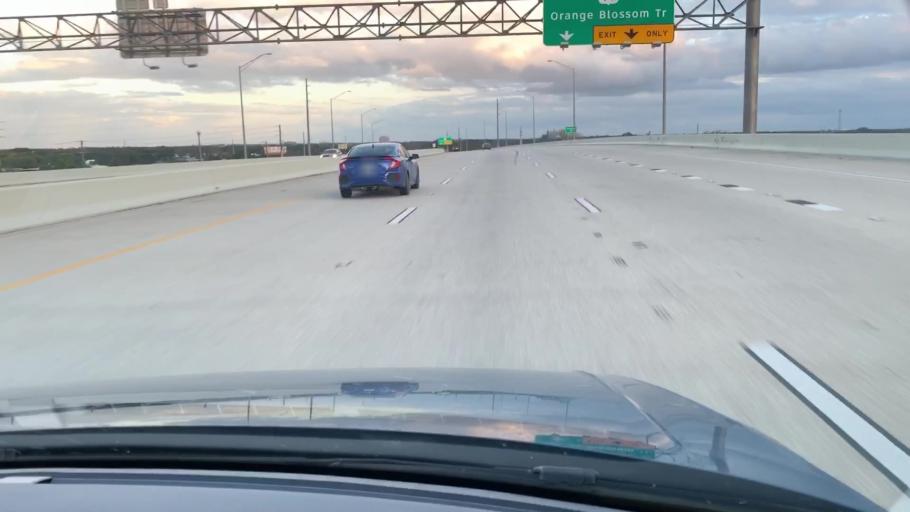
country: US
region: Florida
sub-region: Orange County
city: Lockhart
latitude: 28.6335
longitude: -81.4608
